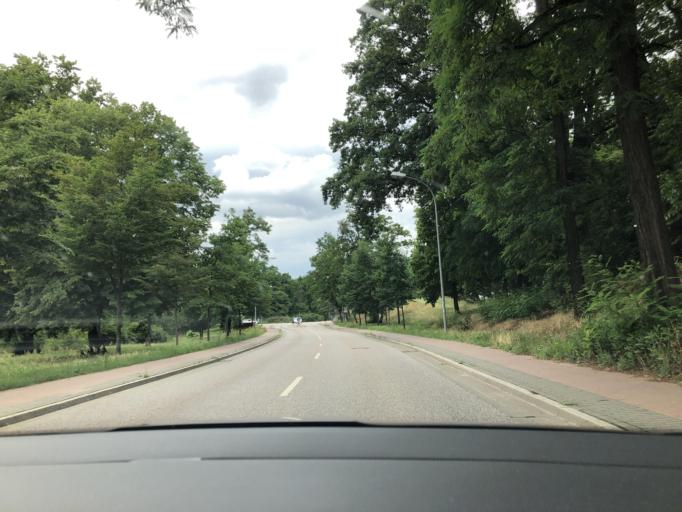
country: DE
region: Saxony-Anhalt
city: Zerbst
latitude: 51.9703
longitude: 12.0915
